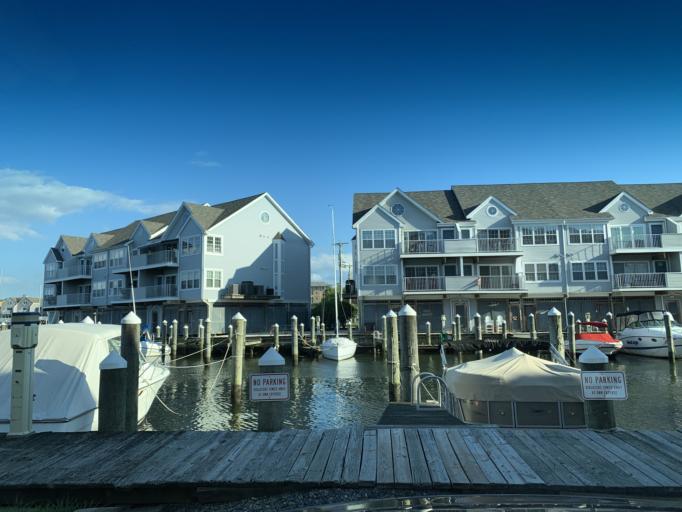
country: US
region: Maryland
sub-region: Harford County
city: Havre de Grace
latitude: 39.5453
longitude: -76.0855
